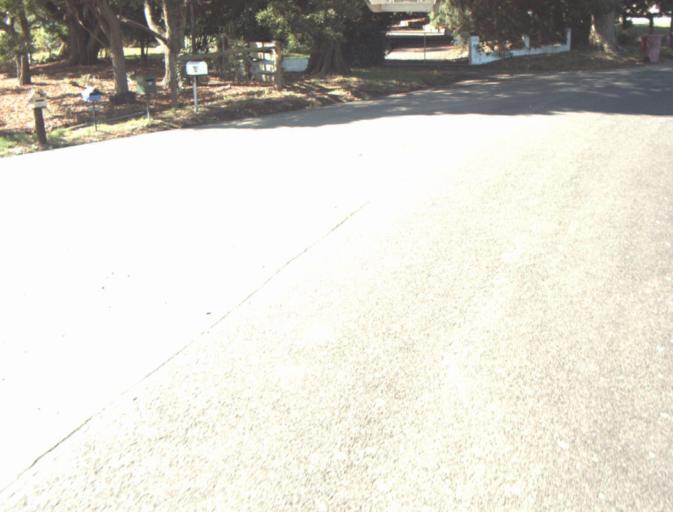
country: AU
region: Tasmania
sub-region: Launceston
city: Mayfield
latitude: -41.2861
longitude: 147.2144
